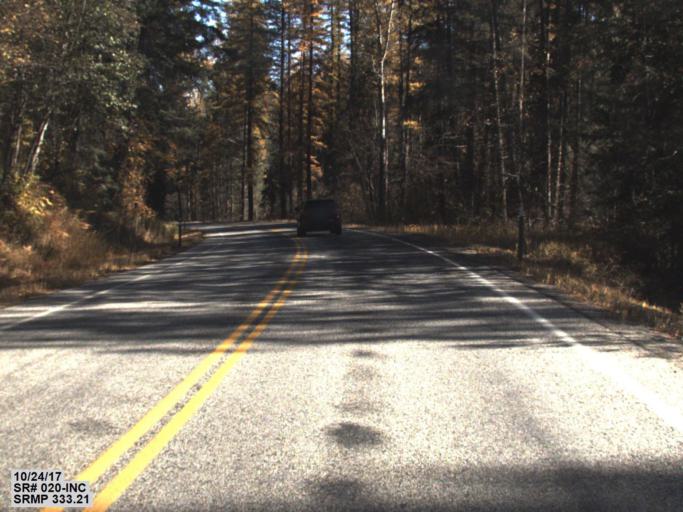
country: US
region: Washington
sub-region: Stevens County
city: Kettle Falls
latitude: 48.5783
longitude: -118.2665
